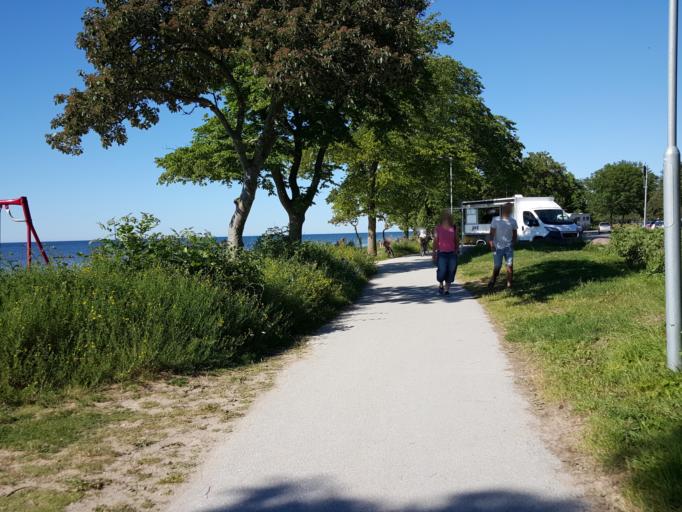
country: SE
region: Gotland
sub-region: Gotland
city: Visby
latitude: 57.6536
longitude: 18.3047
